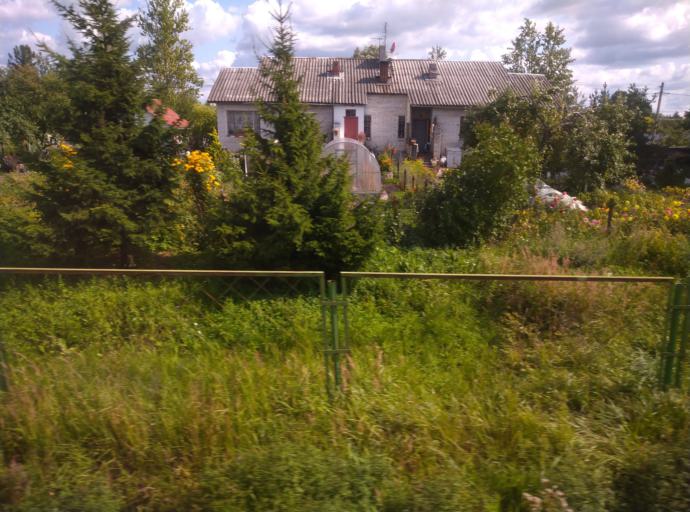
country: RU
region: Leningrad
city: Krasnyy Bor
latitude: 59.6823
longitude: 30.6986
